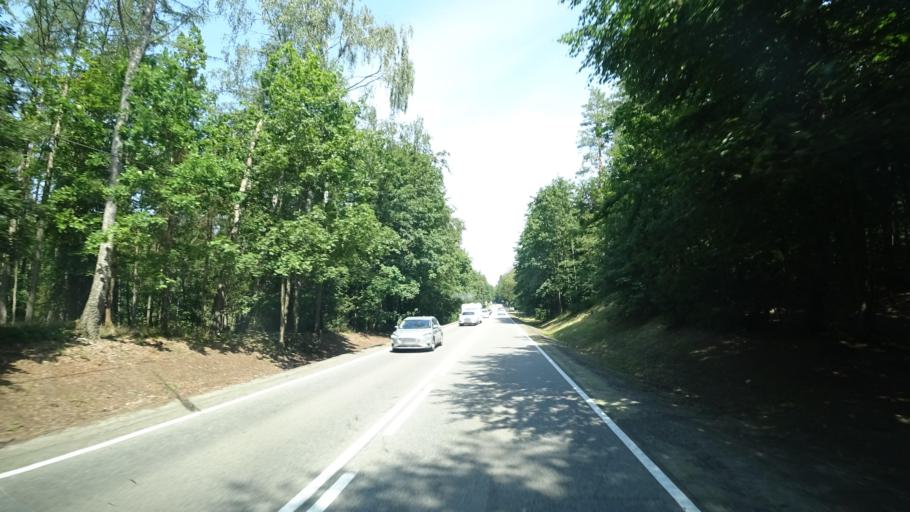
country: PL
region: Pomeranian Voivodeship
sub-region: Powiat koscierski
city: Grabowo Koscierskie
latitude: 54.2133
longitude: 18.1159
